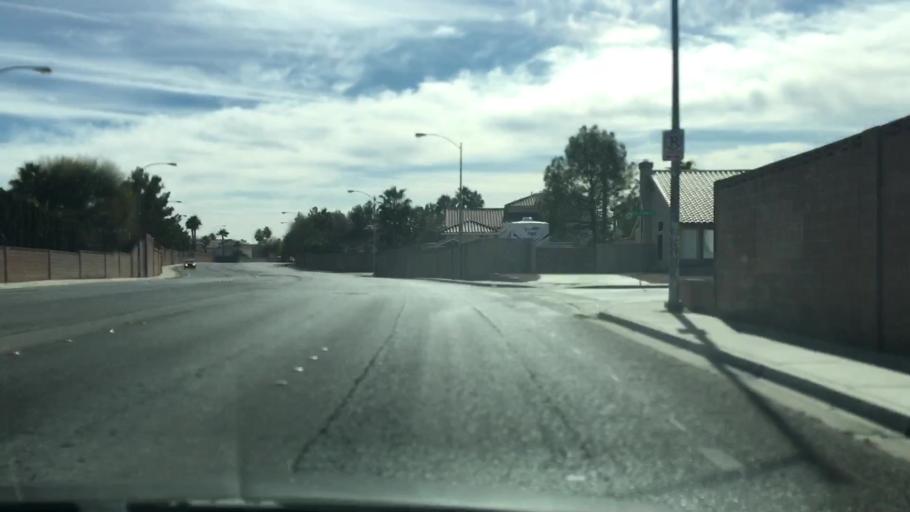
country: US
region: Nevada
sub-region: Clark County
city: Whitney
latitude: 36.0392
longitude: -115.1278
